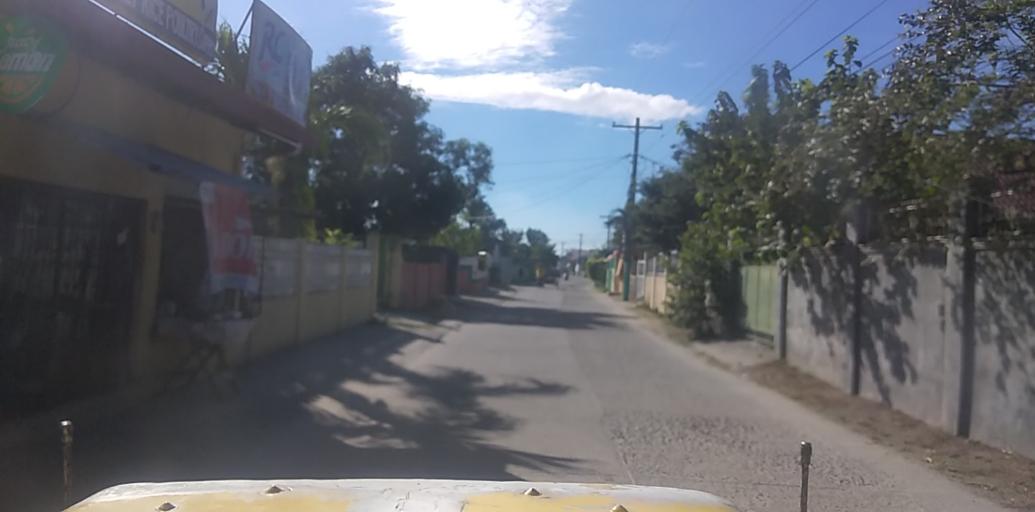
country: PH
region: Central Luzon
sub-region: Province of Pampanga
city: San Patricio
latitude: 15.1070
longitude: 120.7130
